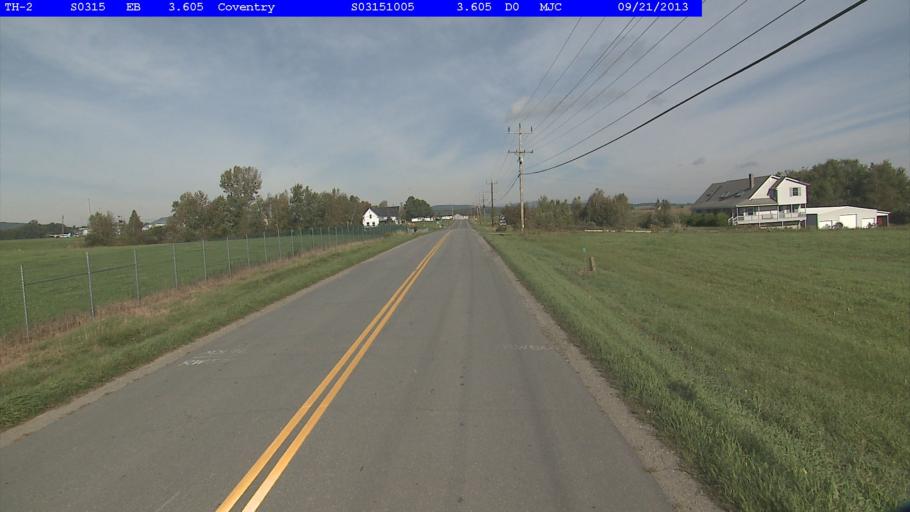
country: US
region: Vermont
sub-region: Orleans County
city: Newport
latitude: 44.8874
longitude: -72.2216
